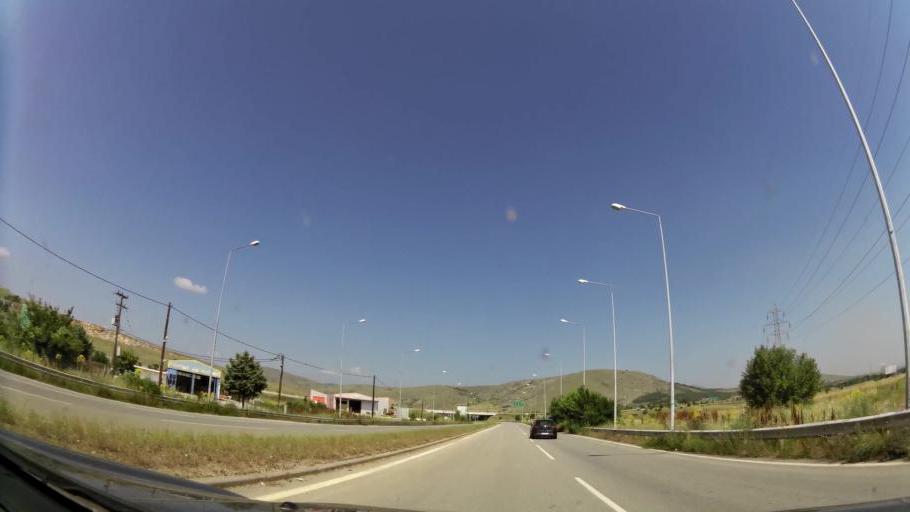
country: GR
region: West Macedonia
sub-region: Nomos Kozanis
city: Koila
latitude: 40.3429
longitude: 21.8096
